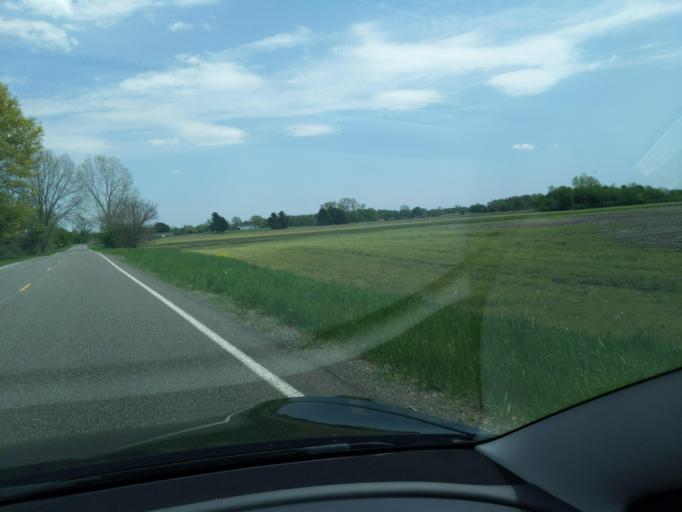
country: US
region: Michigan
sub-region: Ingham County
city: Stockbridge
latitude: 42.4899
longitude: -84.2850
